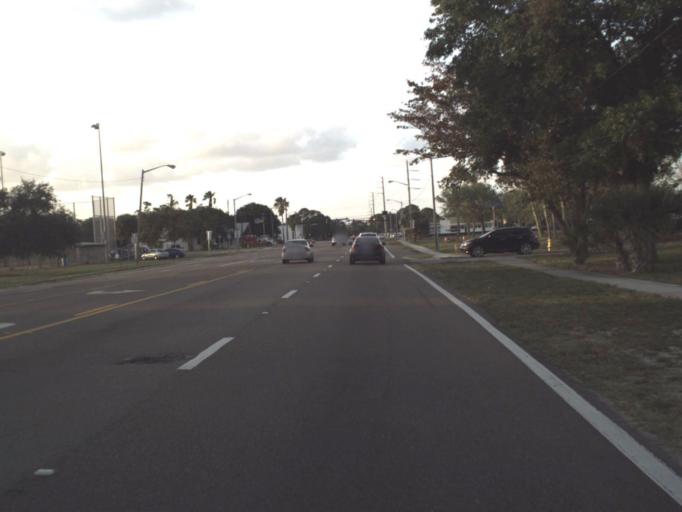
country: US
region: Florida
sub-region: Brevard County
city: Rockledge
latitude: 28.3528
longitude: -80.7425
